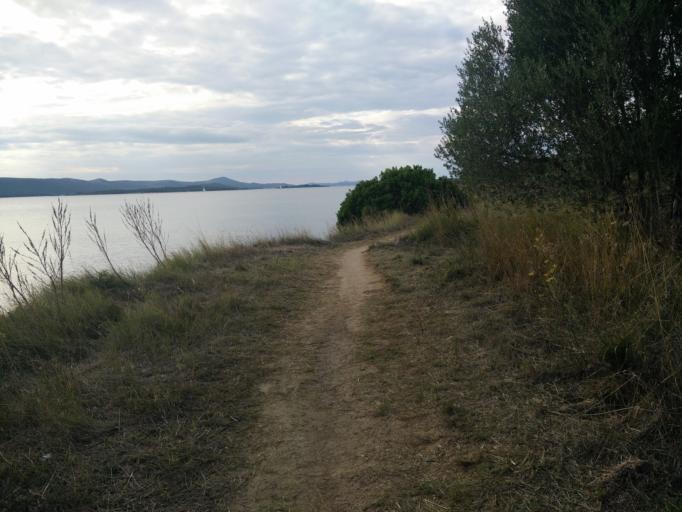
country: HR
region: Zadarska
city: Biograd na Moru
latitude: 43.9494
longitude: 15.4417
